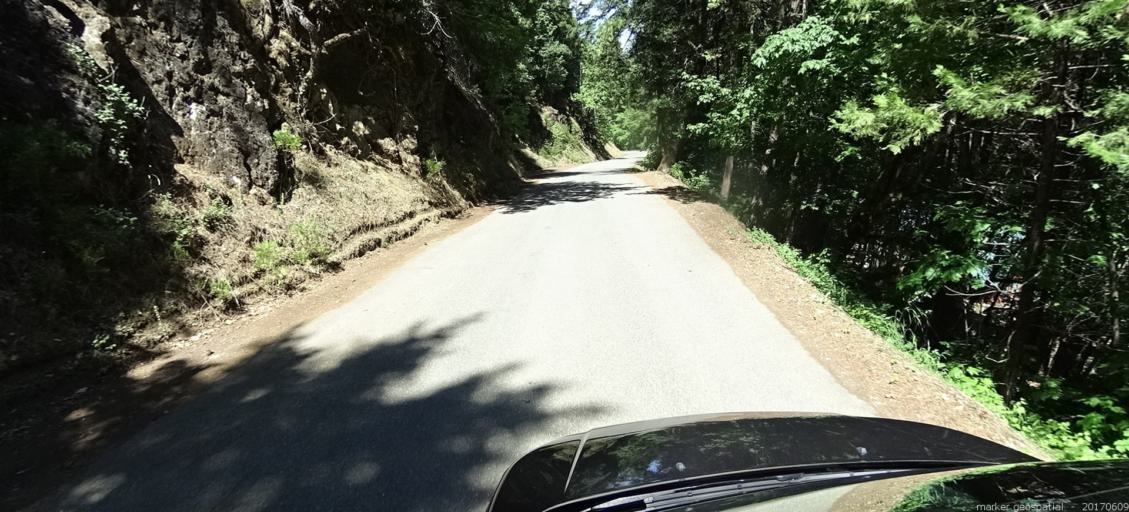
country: US
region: California
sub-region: Siskiyou County
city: Yreka
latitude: 41.4273
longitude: -122.9226
